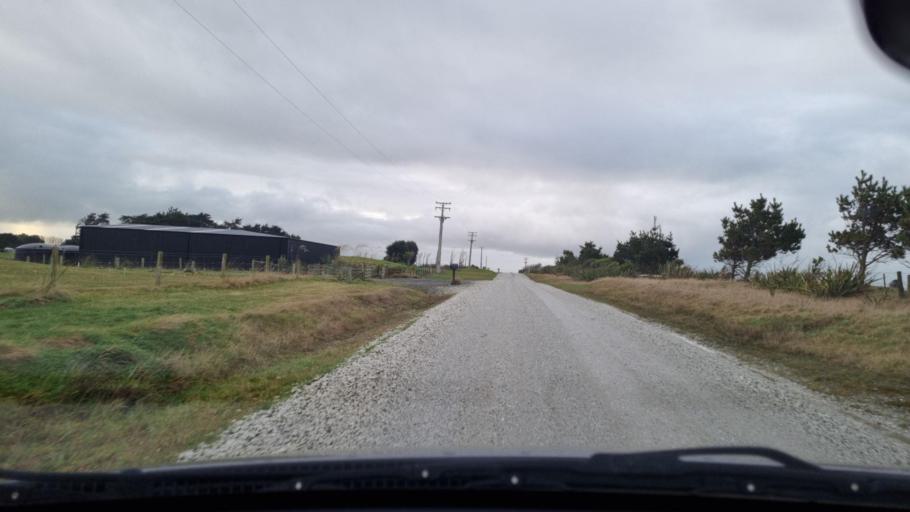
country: NZ
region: Southland
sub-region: Invercargill City
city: Invercargill
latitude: -46.4127
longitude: 168.2634
